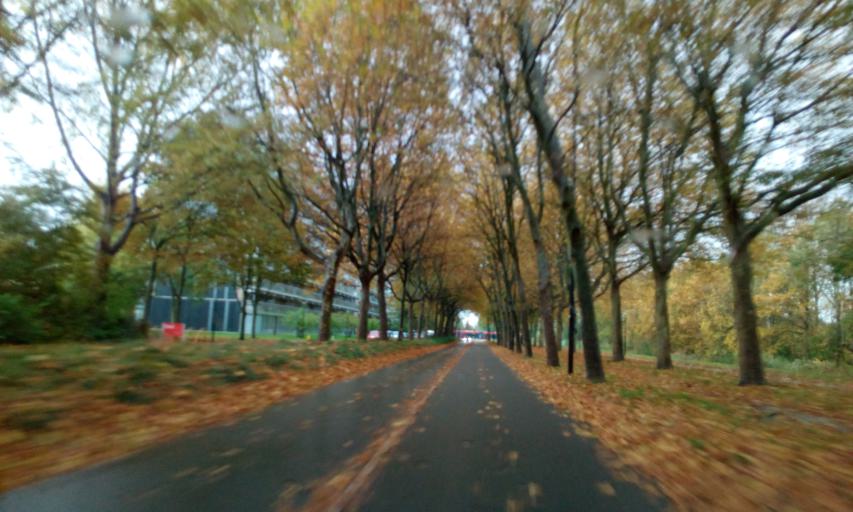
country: NL
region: South Holland
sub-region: Gemeente Rijswijk
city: Rijswijk
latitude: 52.0263
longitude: 4.3084
